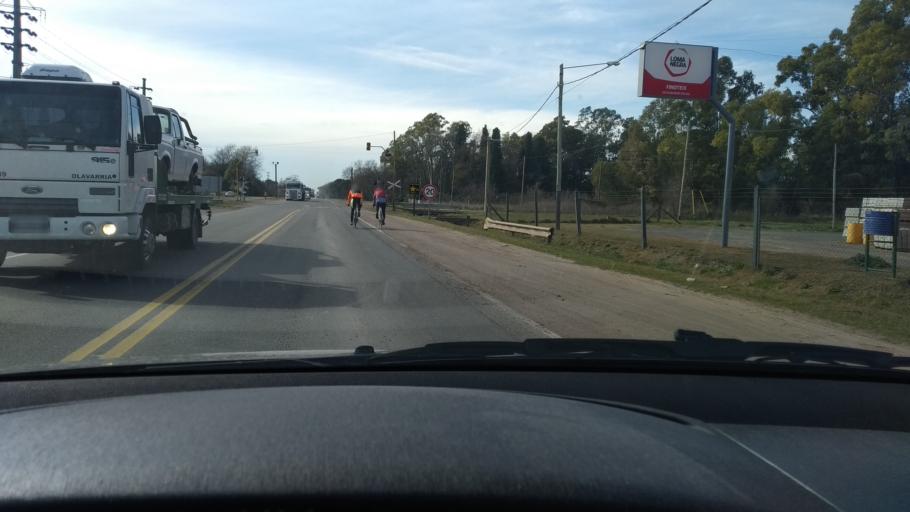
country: AR
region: Buenos Aires
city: Olavarria
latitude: -36.9613
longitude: -60.2610
